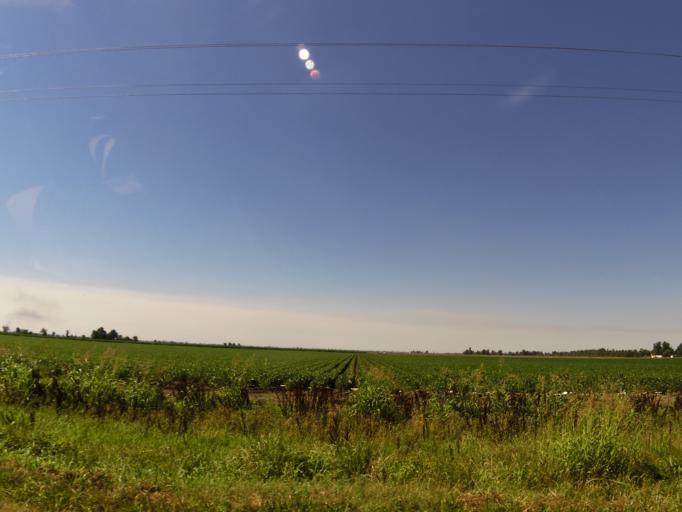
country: US
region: Missouri
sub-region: New Madrid County
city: Gideon
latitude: 36.5537
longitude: -89.8035
